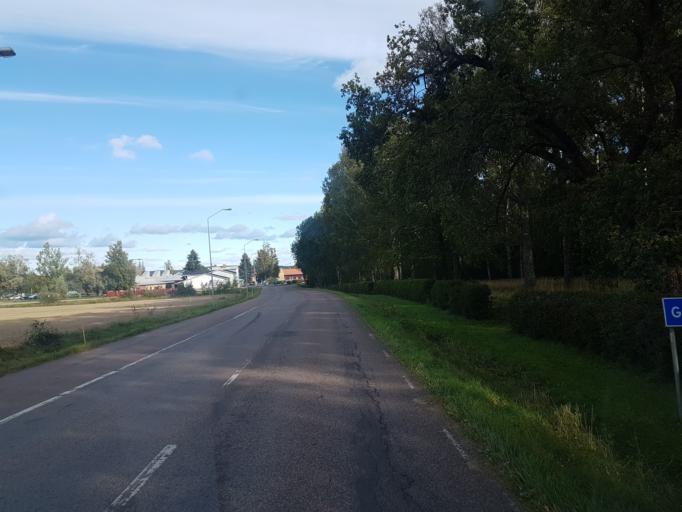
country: SE
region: Dalarna
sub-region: Borlange Kommun
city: Ornas
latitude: 60.4145
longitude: 15.5991
